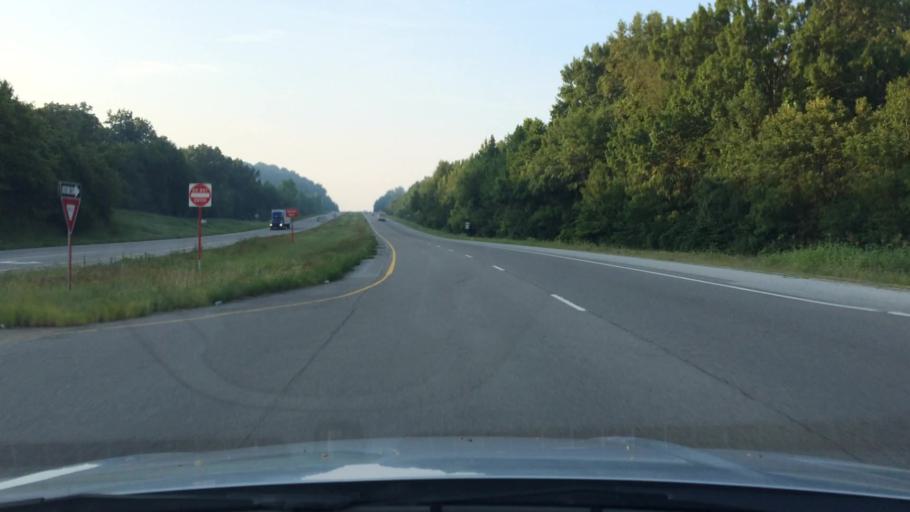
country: US
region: Tennessee
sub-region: Giles County
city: Pulaski
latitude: 35.1883
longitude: -87.0646
